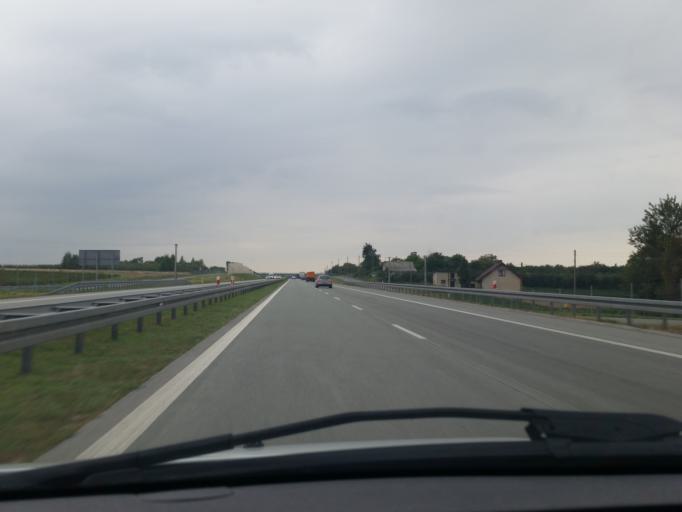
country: PL
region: Lodz Voivodeship
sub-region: Powiat skierniewicki
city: Kowiesy
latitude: 51.8820
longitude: 20.4047
